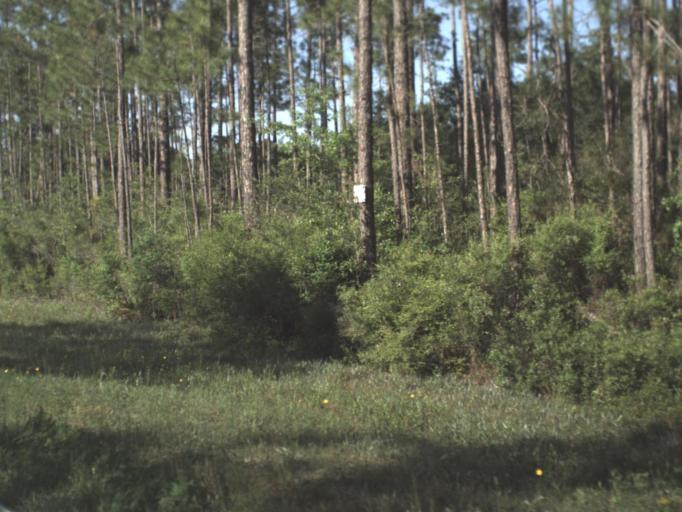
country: US
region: Florida
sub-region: Gulf County
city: Wewahitchka
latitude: 30.0337
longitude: -84.9836
